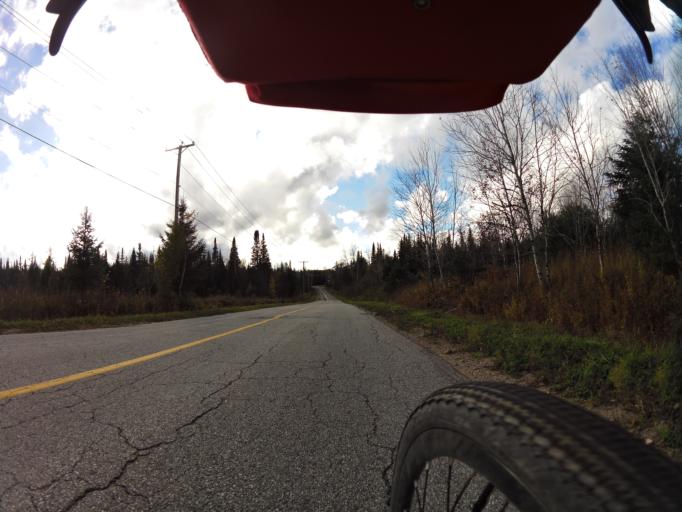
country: CA
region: Quebec
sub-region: Outaouais
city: Wakefield
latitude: 45.6982
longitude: -76.0966
